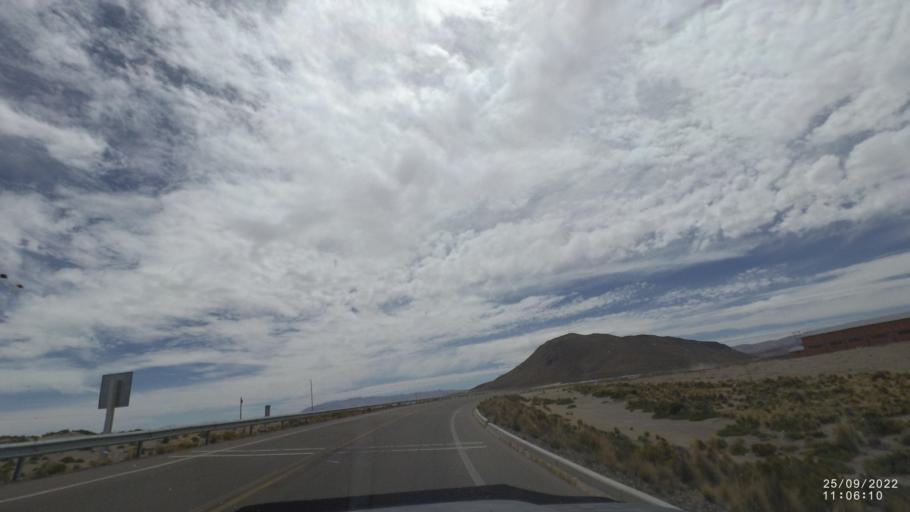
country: BO
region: Oruro
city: Challapata
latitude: -19.3590
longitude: -66.8670
